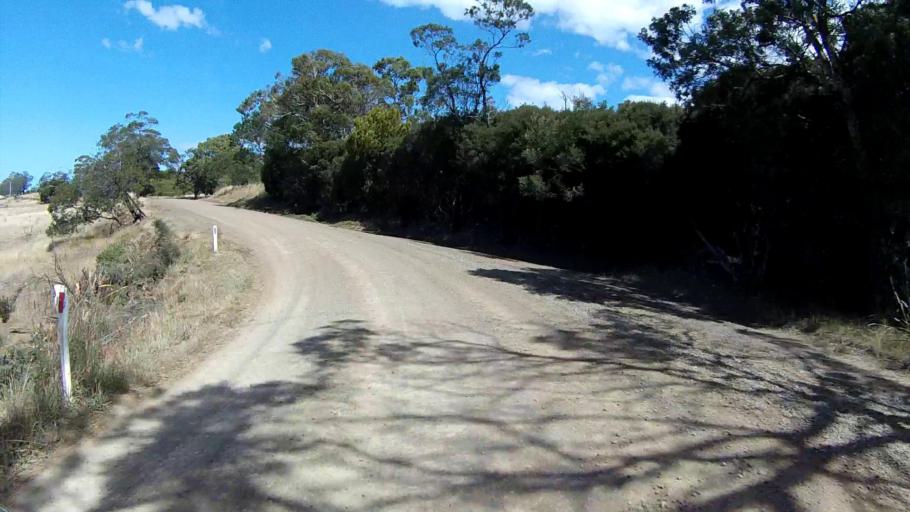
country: AU
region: Tasmania
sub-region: Break O'Day
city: St Helens
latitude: -41.9707
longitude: 148.0728
